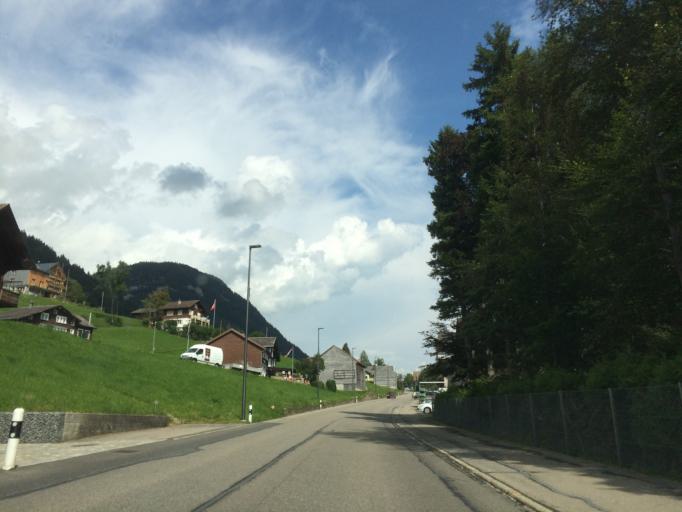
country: CH
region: Saint Gallen
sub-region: Wahlkreis Toggenburg
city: Wildhaus
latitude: 47.2021
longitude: 9.3429
